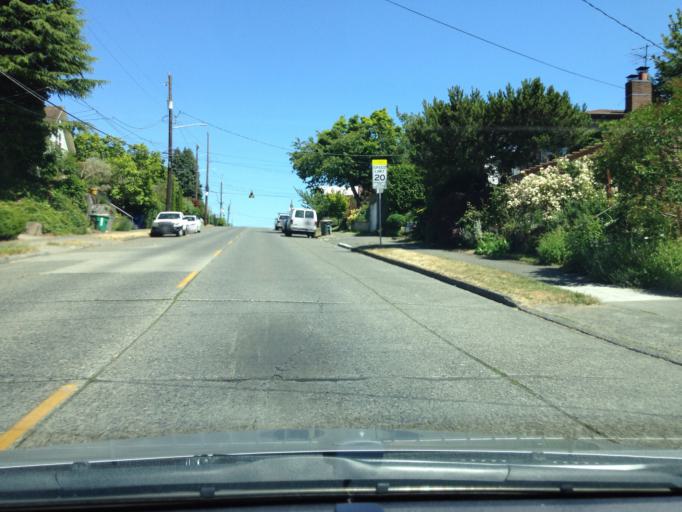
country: US
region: Washington
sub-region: King County
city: Mercer Island
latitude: 47.5512
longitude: -122.2823
